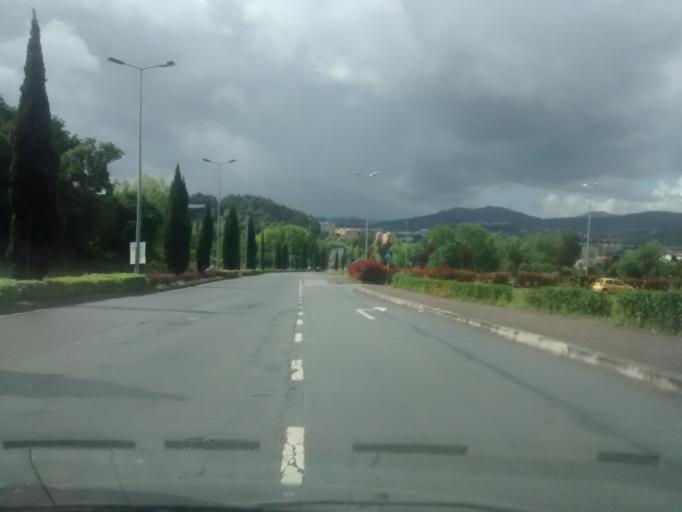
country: PT
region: Braga
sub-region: Braga
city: Braga
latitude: 41.5693
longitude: -8.4274
